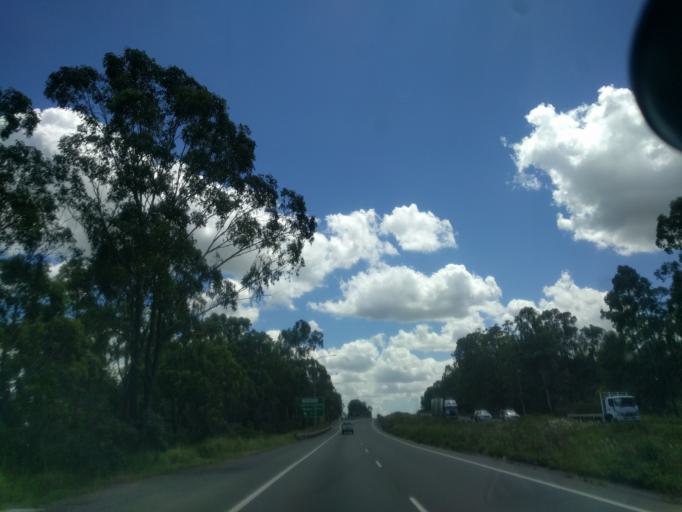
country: AU
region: Queensland
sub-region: Ipswich
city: Riverview
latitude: -27.6033
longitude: 152.8313
